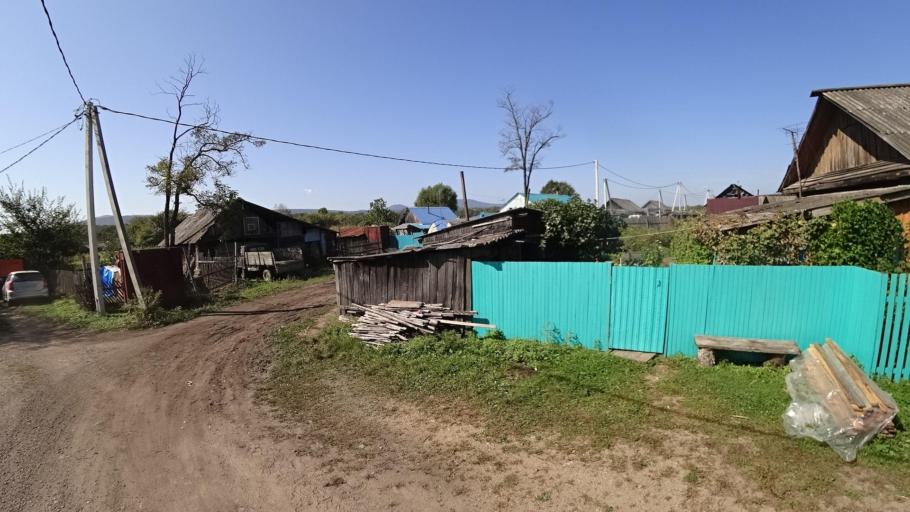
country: RU
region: Jewish Autonomous Oblast
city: Bira
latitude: 48.9928
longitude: 132.4573
